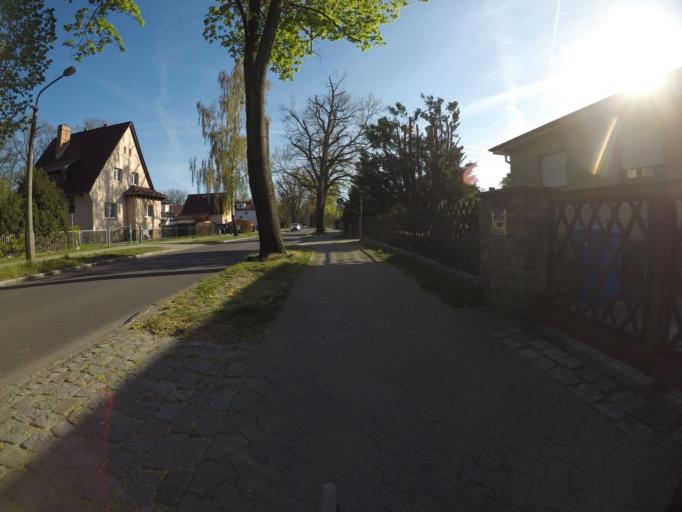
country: DE
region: Brandenburg
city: Neuenhagen
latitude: 52.5157
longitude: 13.7084
